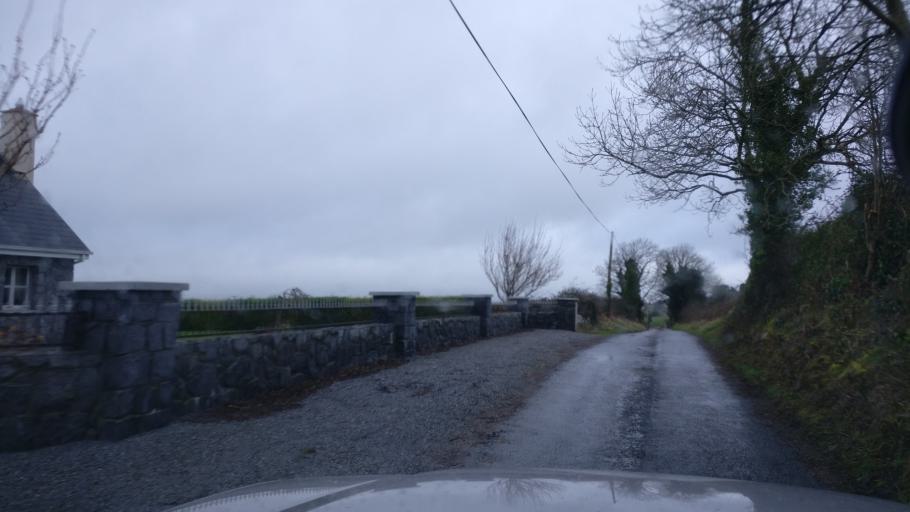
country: IE
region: Connaught
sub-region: County Galway
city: Loughrea
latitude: 53.1691
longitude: -8.6113
